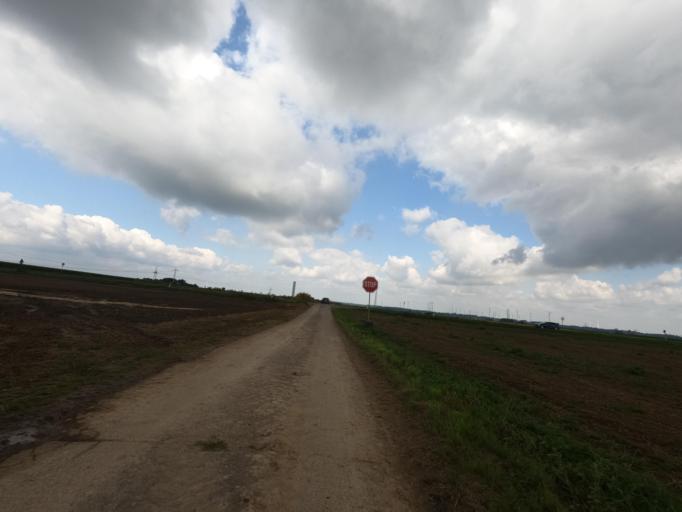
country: DE
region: North Rhine-Westphalia
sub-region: Regierungsbezirk Koln
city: Linnich
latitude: 50.9836
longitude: 6.2449
